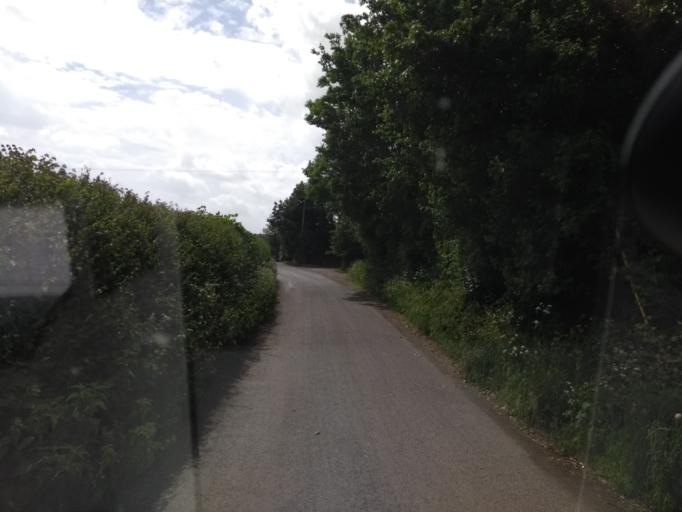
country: GB
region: England
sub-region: Somerset
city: Bridgwater
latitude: 51.1771
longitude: -3.0786
